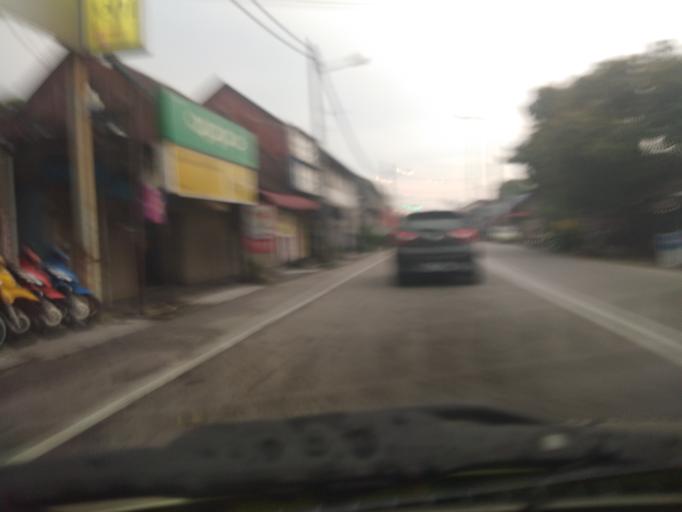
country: MY
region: Penang
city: Permatang Kuching
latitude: 5.4486
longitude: 100.3969
